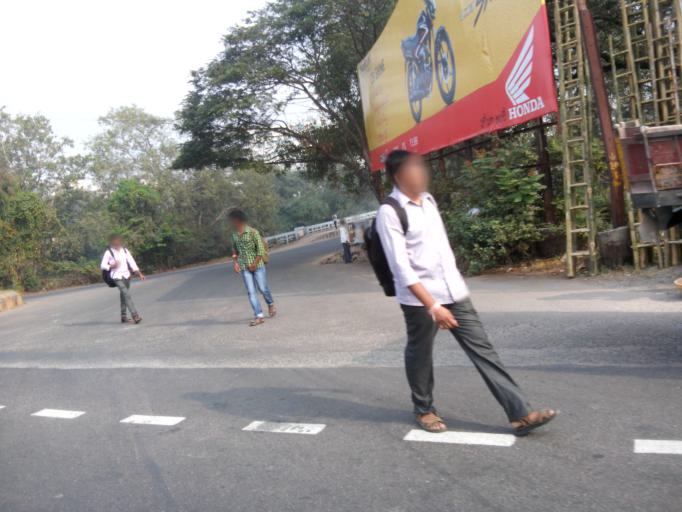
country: IN
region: Andhra Pradesh
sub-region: Krishna
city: Vijayawada
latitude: 16.5092
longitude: 80.6209
